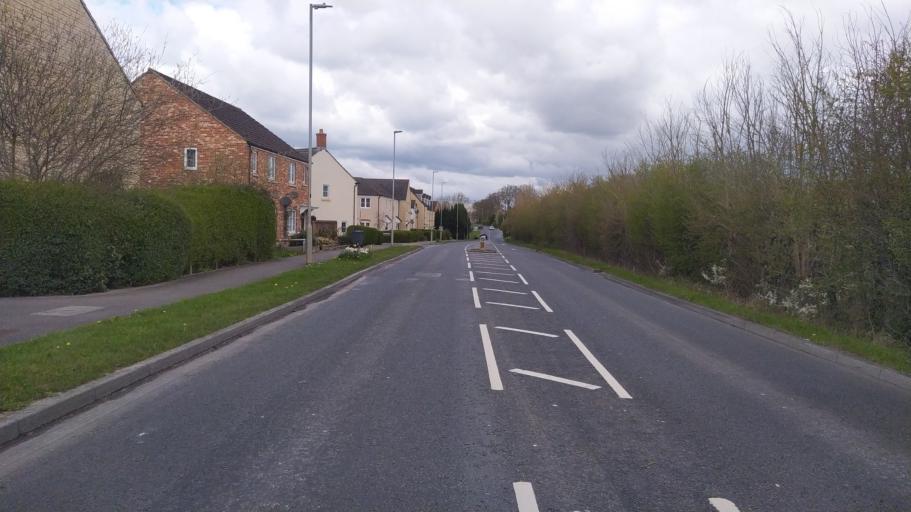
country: GB
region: England
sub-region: Wiltshire
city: Trowbridge
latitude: 51.3139
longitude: -2.1911
